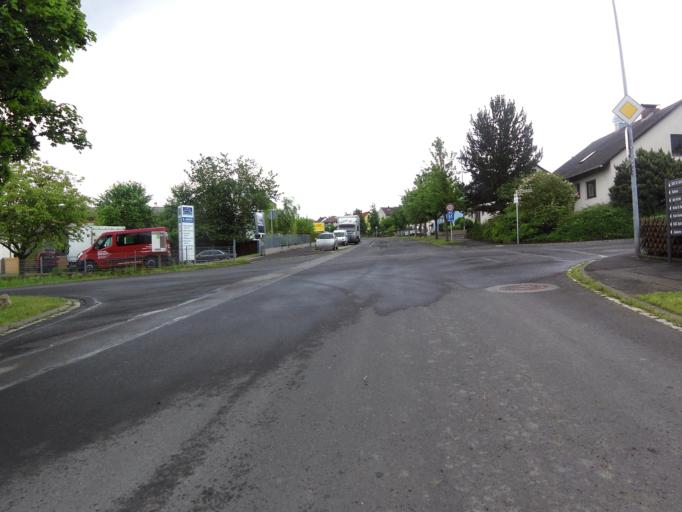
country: DE
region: Bavaria
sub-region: Regierungsbezirk Unterfranken
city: Waldbuttelbrunn
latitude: 49.7866
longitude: 9.8313
